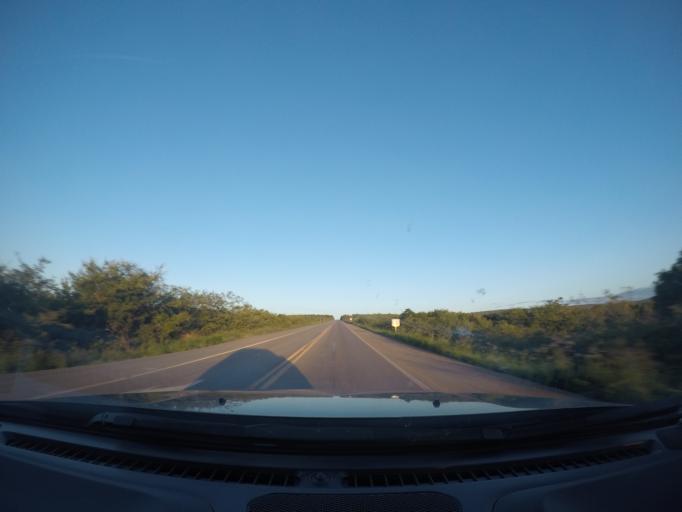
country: BR
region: Bahia
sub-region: Seabra
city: Seabra
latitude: -12.3923
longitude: -41.9168
